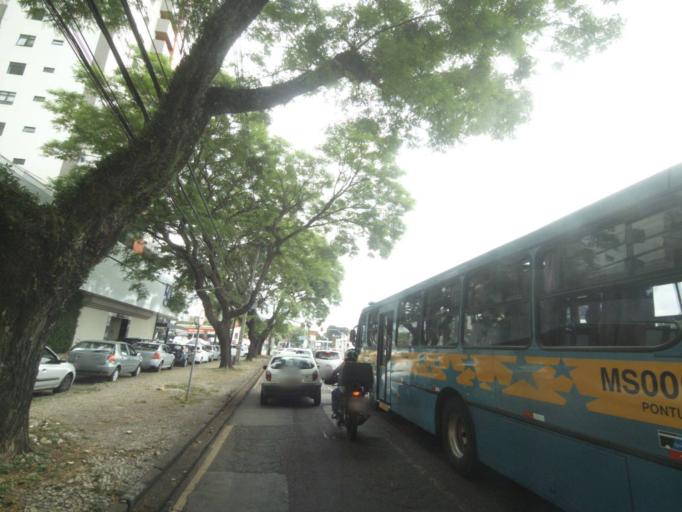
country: BR
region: Parana
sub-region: Curitiba
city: Curitiba
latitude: -25.4345
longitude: -49.3065
